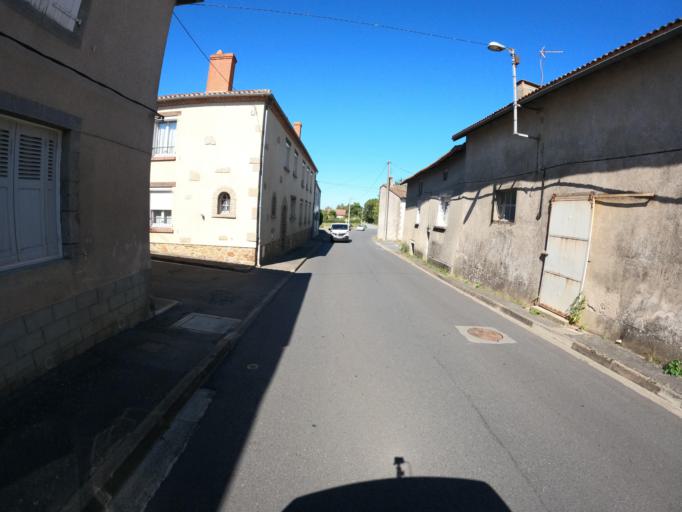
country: FR
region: Limousin
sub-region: Departement de la Haute-Vienne
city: Le Dorat
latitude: 46.2197
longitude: 1.0753
